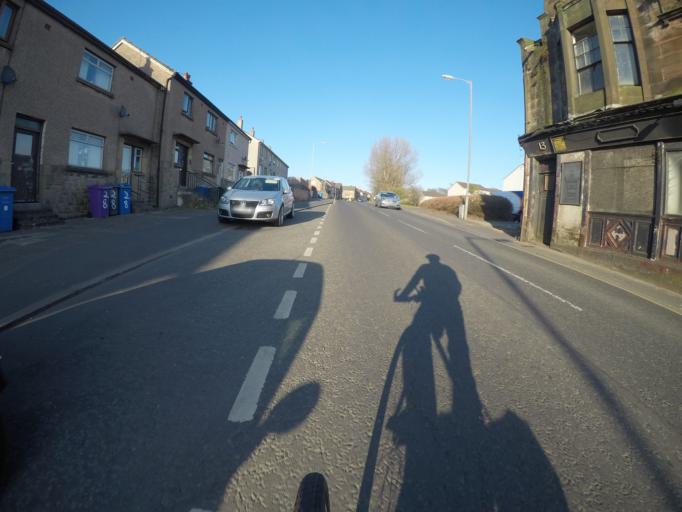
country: GB
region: Scotland
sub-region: North Ayrshire
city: Stevenston
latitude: 55.6413
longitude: -4.7548
